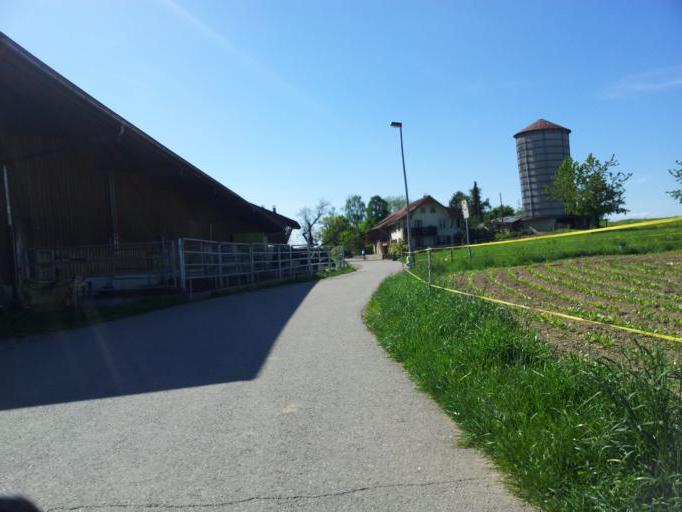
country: CH
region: Zurich
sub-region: Bezirk Dietikon
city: Schlieren / Boden
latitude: 47.3925
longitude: 8.4595
